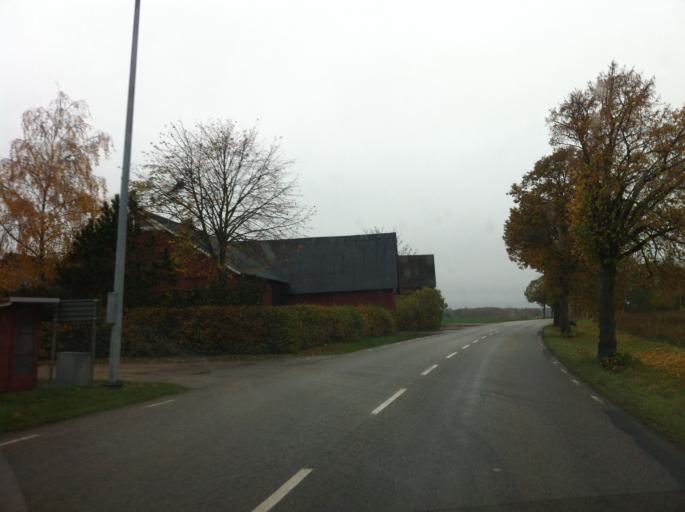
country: SE
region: Skane
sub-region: Kavlinge Kommun
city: Loddekopinge
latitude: 55.8123
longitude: 13.0539
